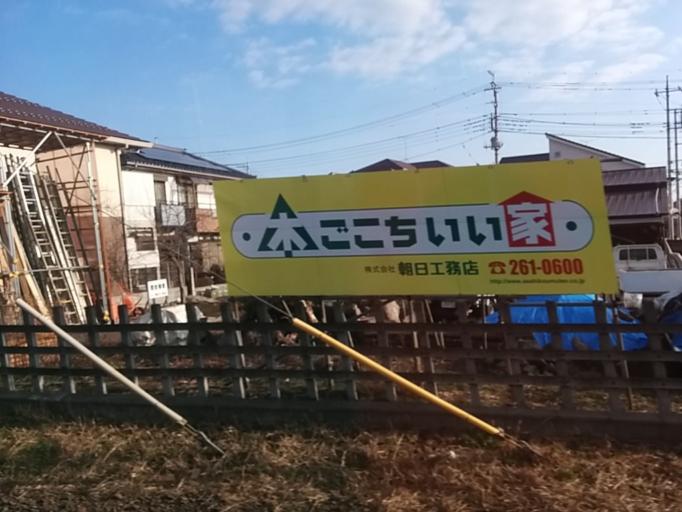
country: JP
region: Saitama
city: Oi
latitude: 35.8569
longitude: 139.5265
